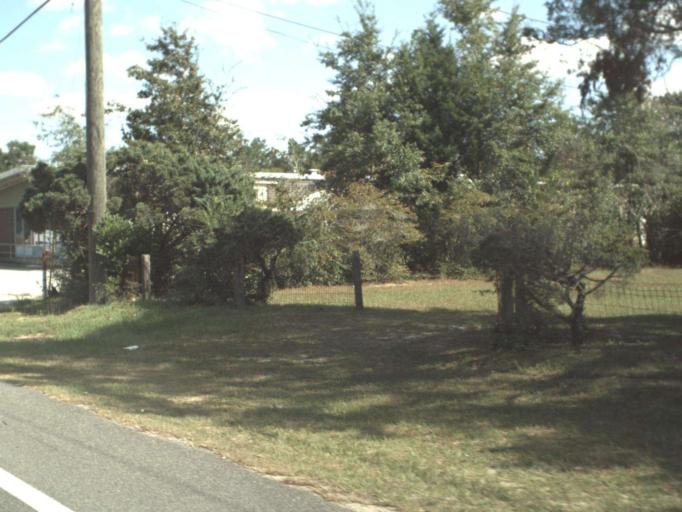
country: US
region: Florida
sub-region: Walton County
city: DeFuniak Springs
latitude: 30.7283
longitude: -86.1147
